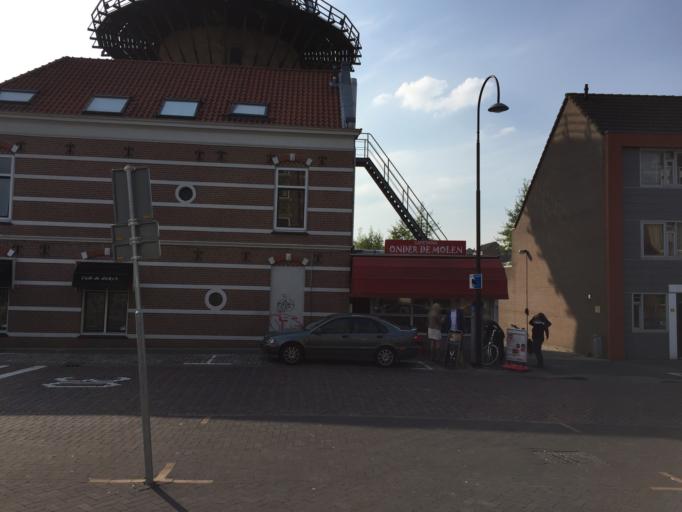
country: NL
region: South Holland
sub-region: Gemeente Dordrecht
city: Dordrecht
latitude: 51.8155
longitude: 4.6794
